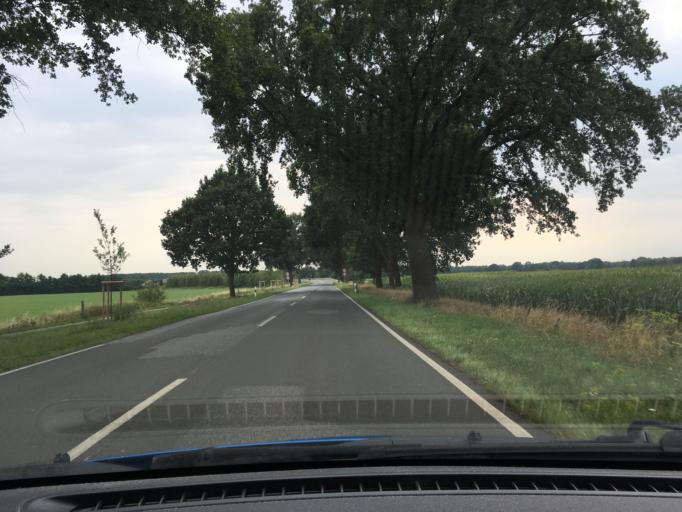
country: DE
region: Lower Saxony
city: Adelheidsdorf
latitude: 52.5399
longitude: 10.0510
